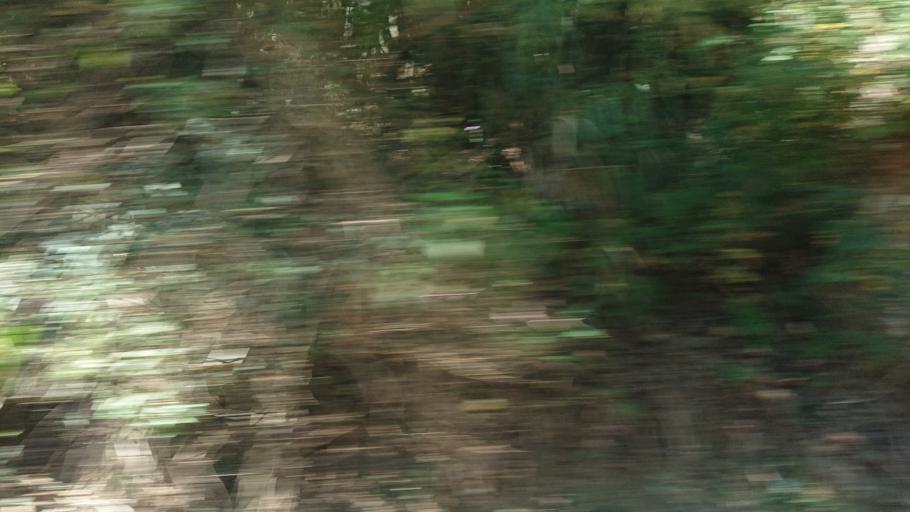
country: TW
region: Taiwan
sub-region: Yunlin
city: Douliu
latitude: 23.5339
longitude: 120.6439
